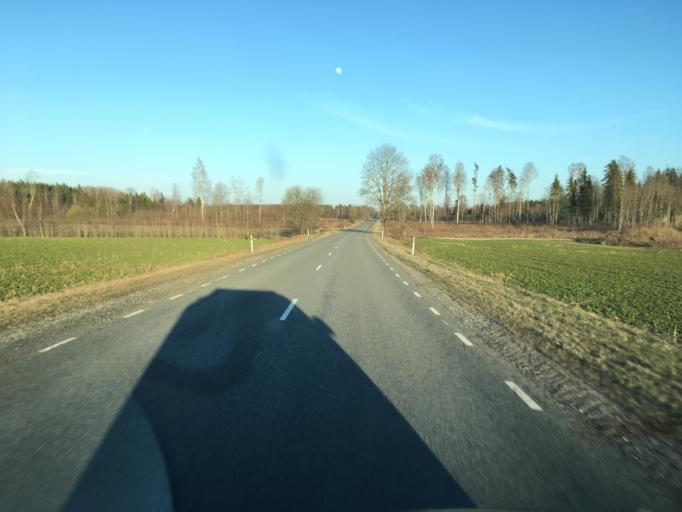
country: EE
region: Raplamaa
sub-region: Rapla vald
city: Rapla
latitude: 59.0740
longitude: 24.8890
